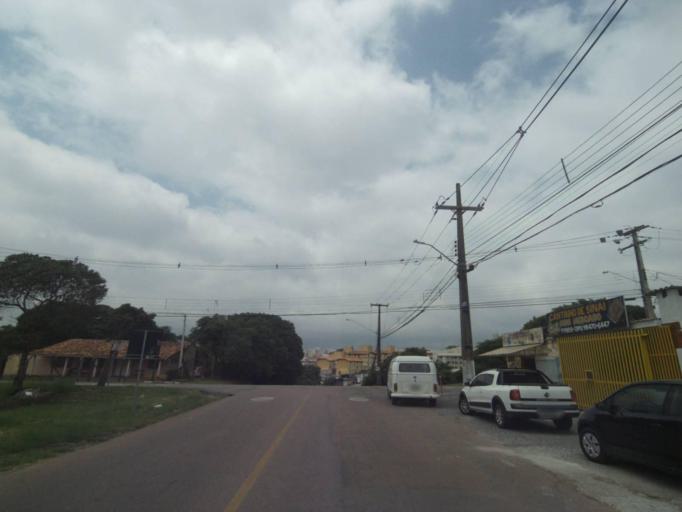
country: BR
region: Parana
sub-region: Curitiba
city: Curitiba
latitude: -25.4903
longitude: -49.3498
